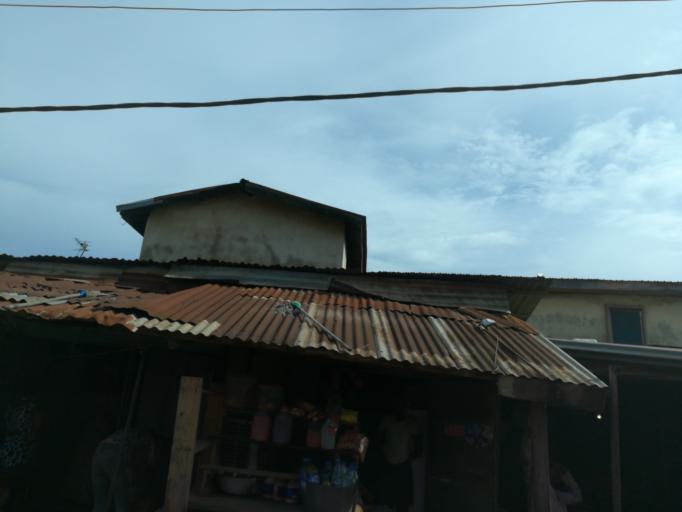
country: NG
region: Lagos
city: Oshodi
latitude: 6.5608
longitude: 3.3472
